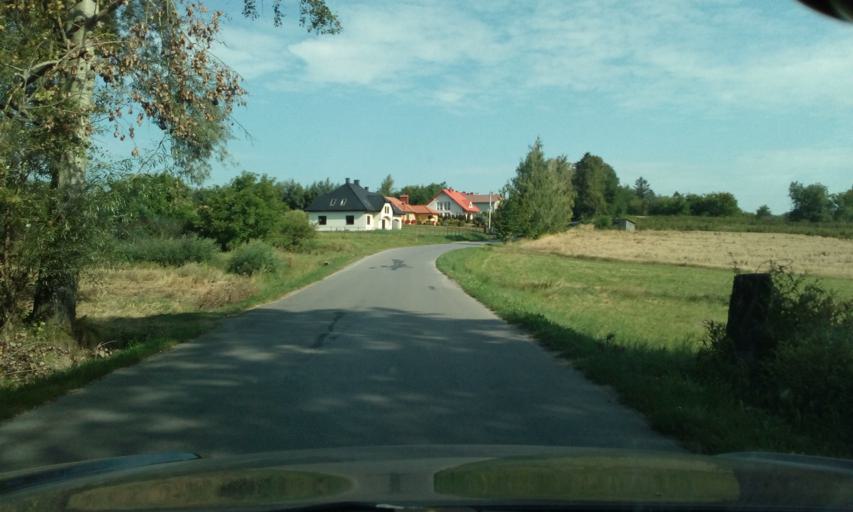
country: PL
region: Subcarpathian Voivodeship
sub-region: Powiat lancucki
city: Wysoka
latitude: 50.0493
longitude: 22.2400
